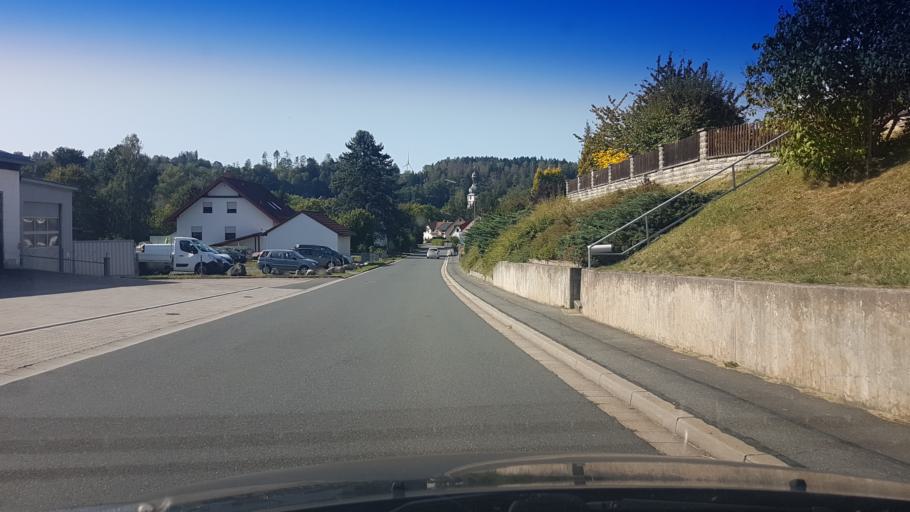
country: DE
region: Bavaria
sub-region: Upper Franconia
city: Marktschorgast
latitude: 50.0946
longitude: 11.6608
